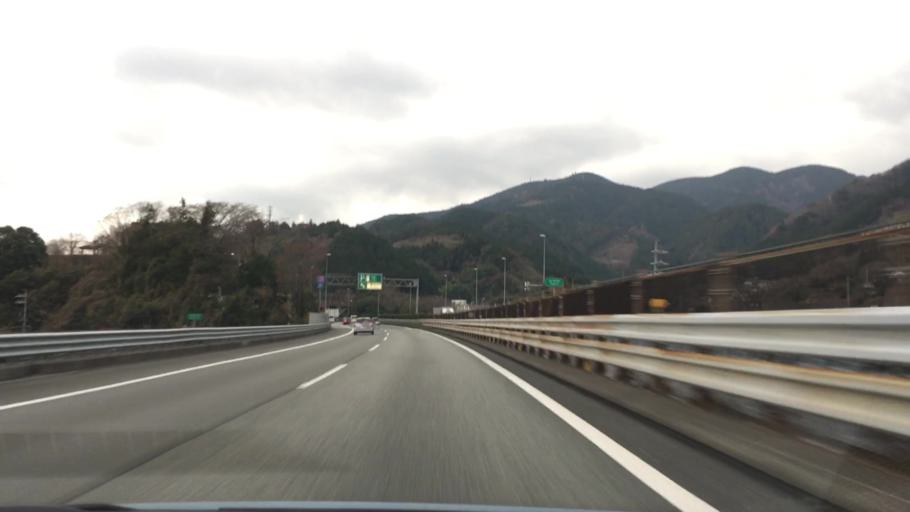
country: JP
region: Shizuoka
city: Fujinomiya
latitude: 35.1612
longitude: 138.6208
